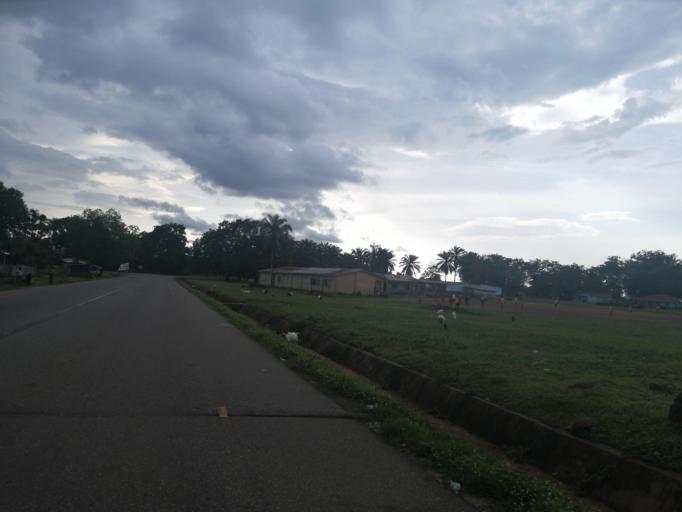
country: SL
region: Northern Province
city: Port Loko
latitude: 8.7751
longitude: -12.7917
